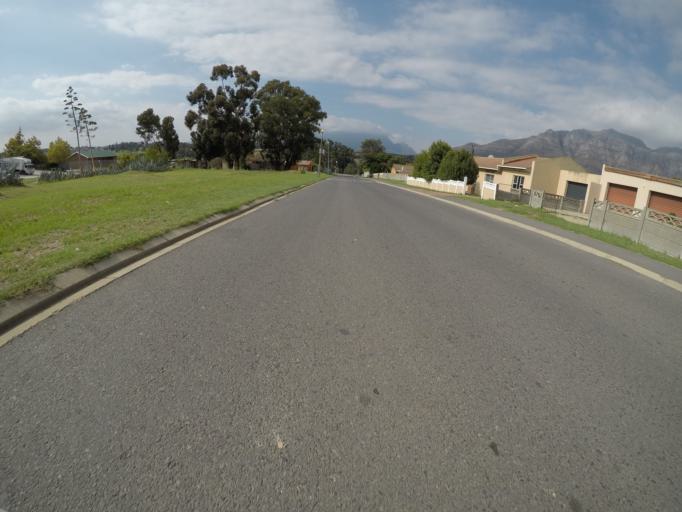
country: ZA
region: Western Cape
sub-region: Cape Winelands District Municipality
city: Stellenbosch
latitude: -33.9775
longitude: 18.8438
